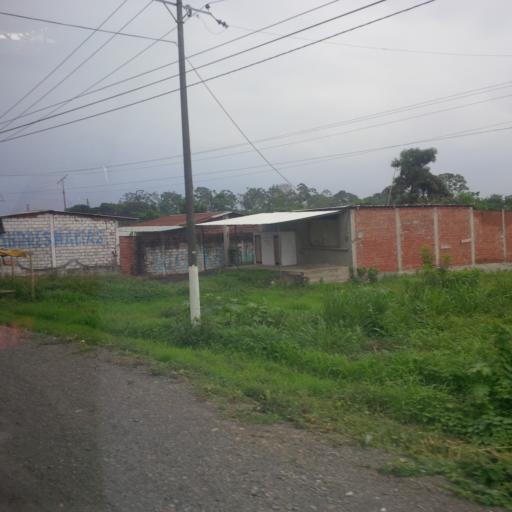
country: EC
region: Canar
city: La Troncal
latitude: -2.3385
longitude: -79.3890
